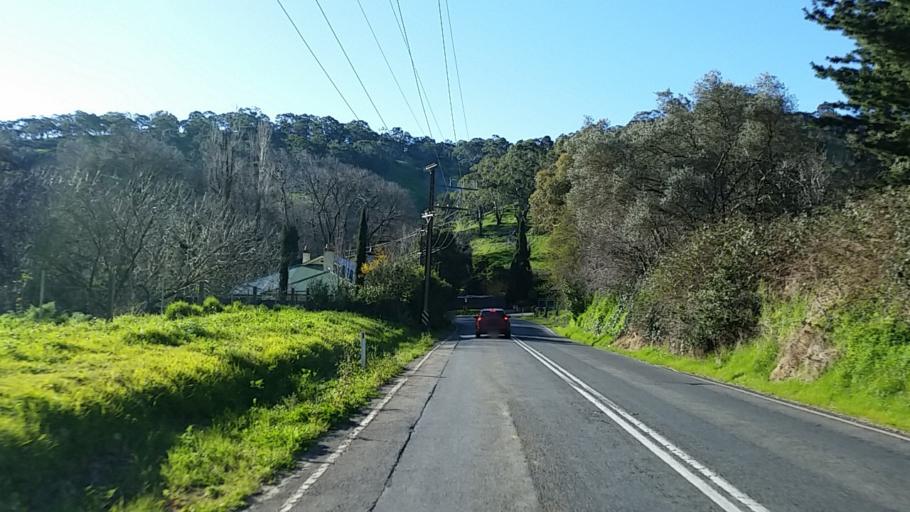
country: AU
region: South Australia
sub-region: Adelaide Hills
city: Adelaide Hills
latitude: -34.9233
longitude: 138.7184
